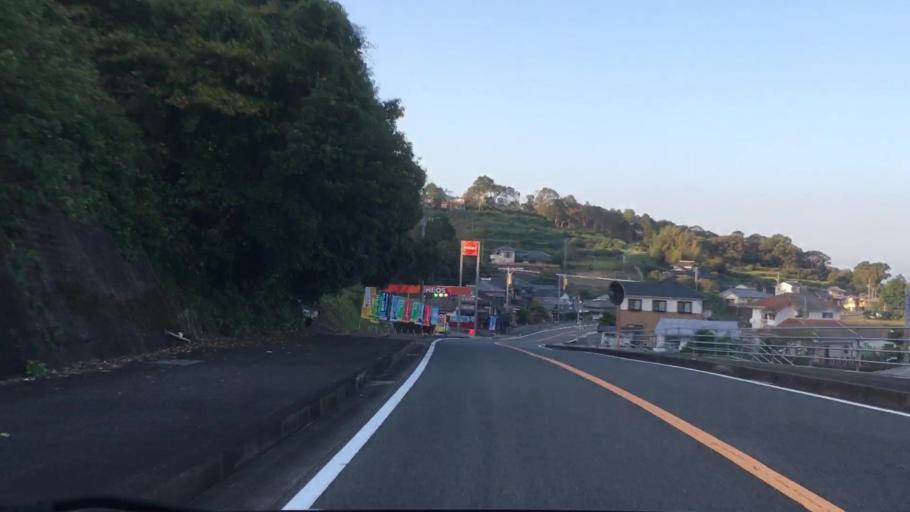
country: JP
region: Nagasaki
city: Sasebo
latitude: 33.0064
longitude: 129.7312
